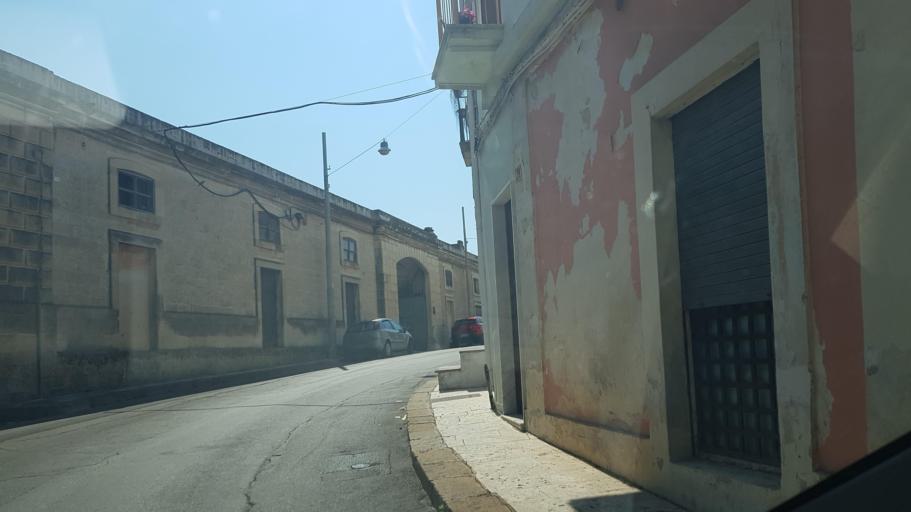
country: IT
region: Apulia
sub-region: Provincia di Lecce
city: Ugento
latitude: 39.9271
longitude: 18.1626
